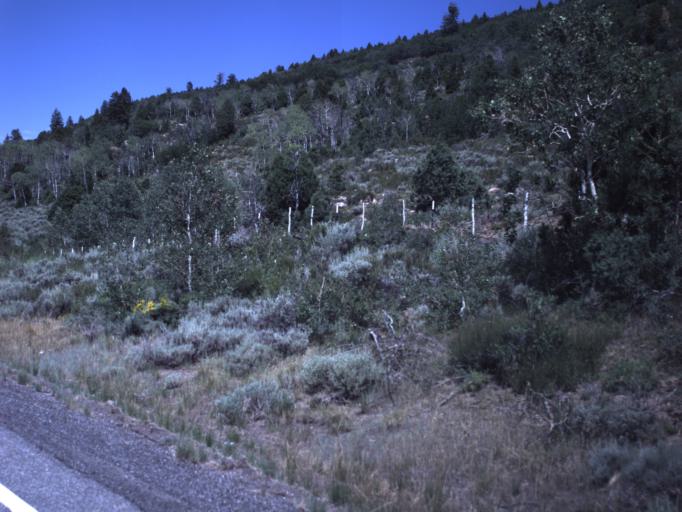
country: US
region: Utah
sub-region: Carbon County
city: Helper
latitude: 39.8571
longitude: -111.0926
